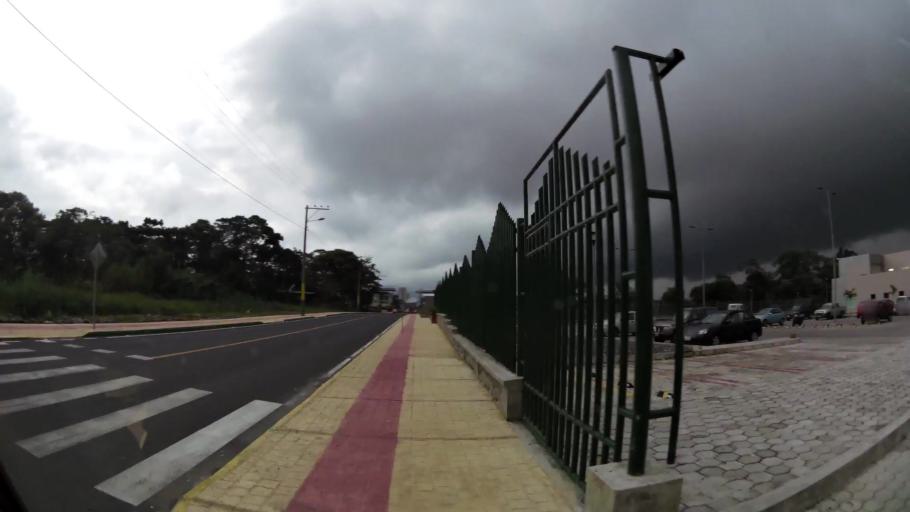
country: EC
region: Pastaza
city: Puyo
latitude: -1.4865
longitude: -78.0110
